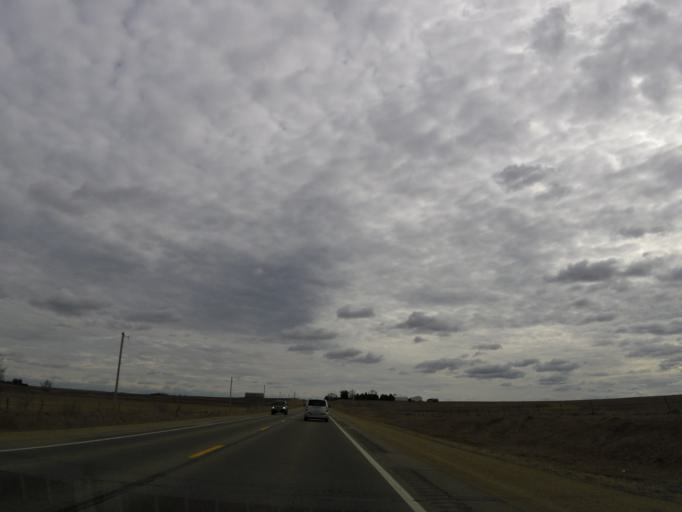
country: US
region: Iowa
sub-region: Chickasaw County
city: New Hampton
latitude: 43.1689
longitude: -92.2987
